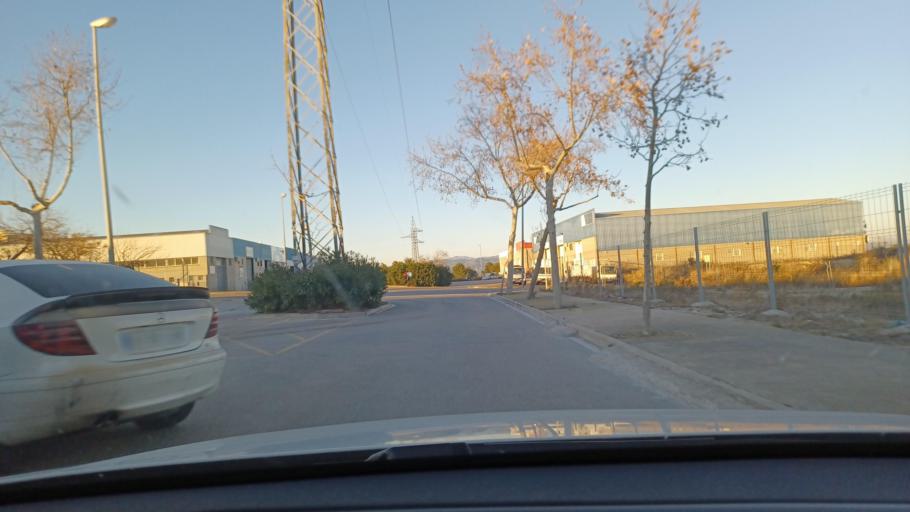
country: ES
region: Catalonia
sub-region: Provincia de Tarragona
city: Amposta
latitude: 40.7040
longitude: 0.5617
